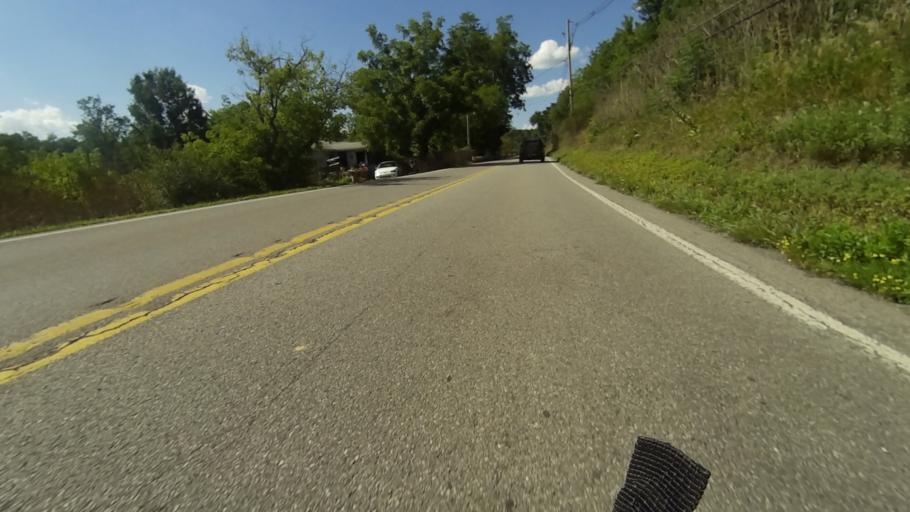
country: US
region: Pennsylvania
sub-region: Blair County
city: Greenwood
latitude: 40.5679
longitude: -78.3433
